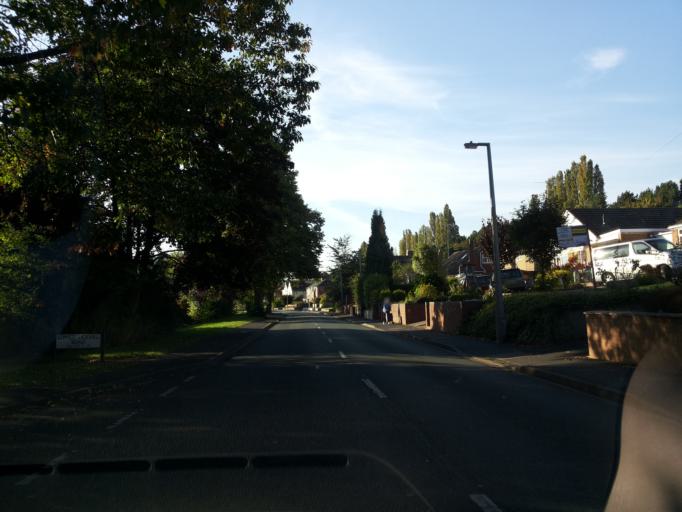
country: GB
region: England
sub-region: Worcestershire
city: Stourport-on-Severn
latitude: 52.3457
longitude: -2.2893
